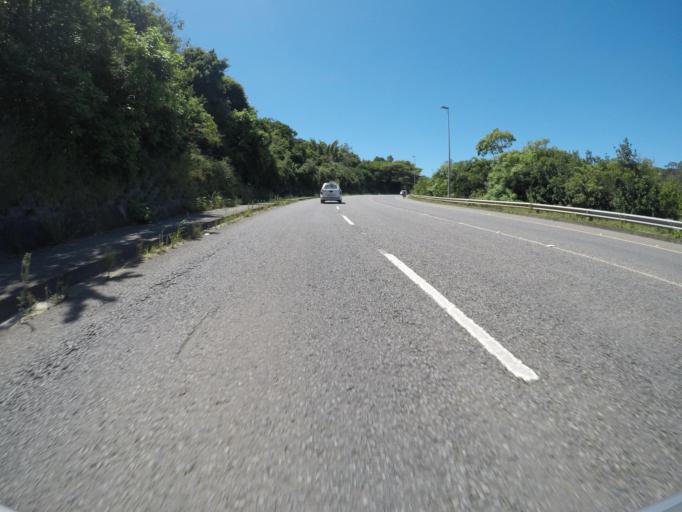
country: ZA
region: Eastern Cape
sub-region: Buffalo City Metropolitan Municipality
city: East London
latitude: -32.9689
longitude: 27.9304
